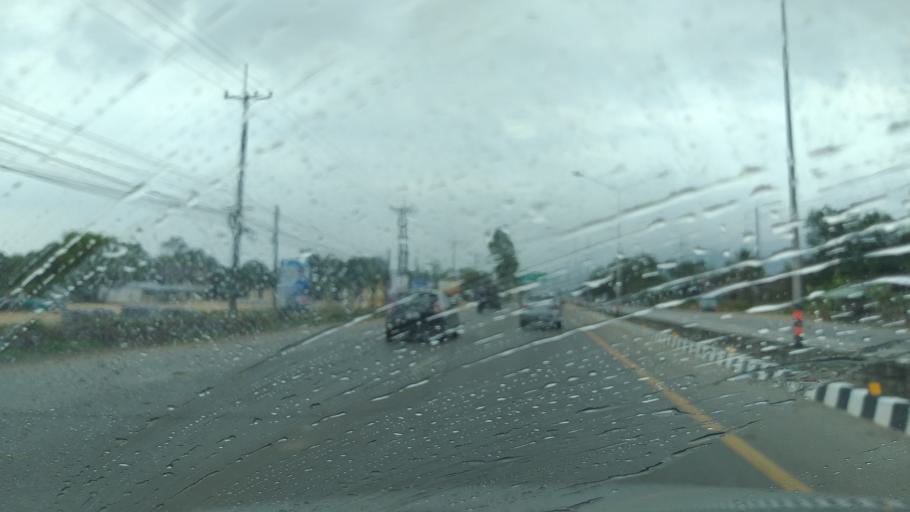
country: TH
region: Chanthaburi
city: Khlung
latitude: 12.4561
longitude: 102.2366
